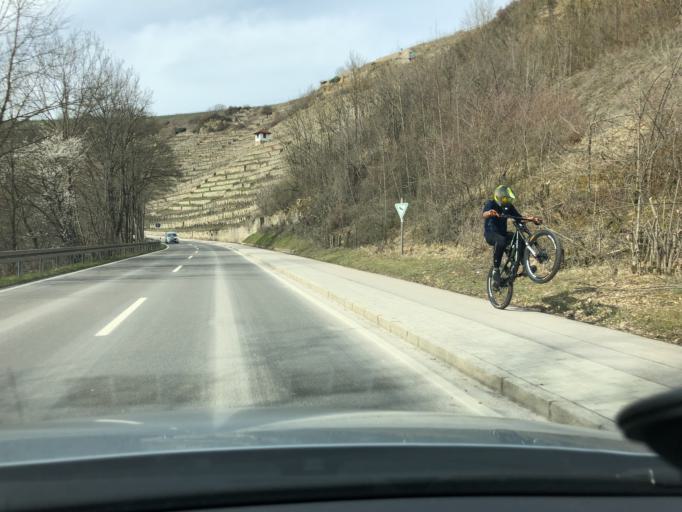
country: DE
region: Baden-Wuerttemberg
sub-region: Karlsruhe Region
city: Illingen
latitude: 48.9374
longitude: 8.9258
